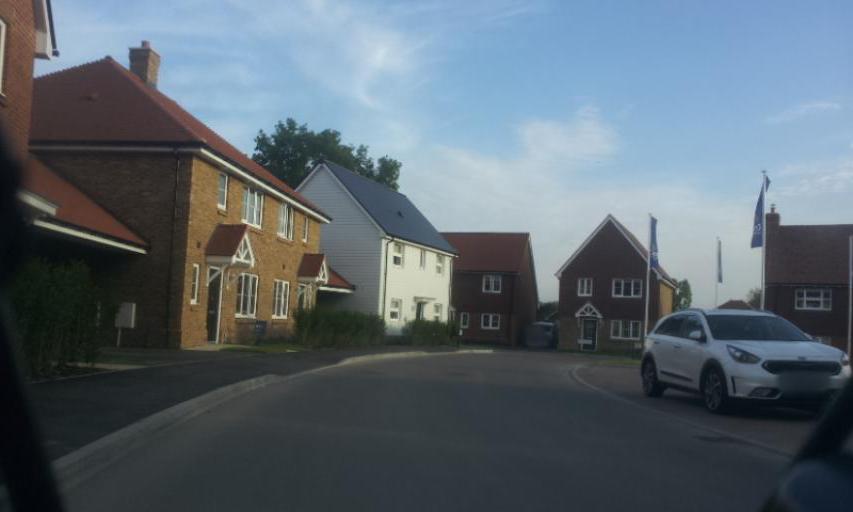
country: GB
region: England
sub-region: Kent
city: Harrietsham
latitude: 51.2417
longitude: 0.6797
